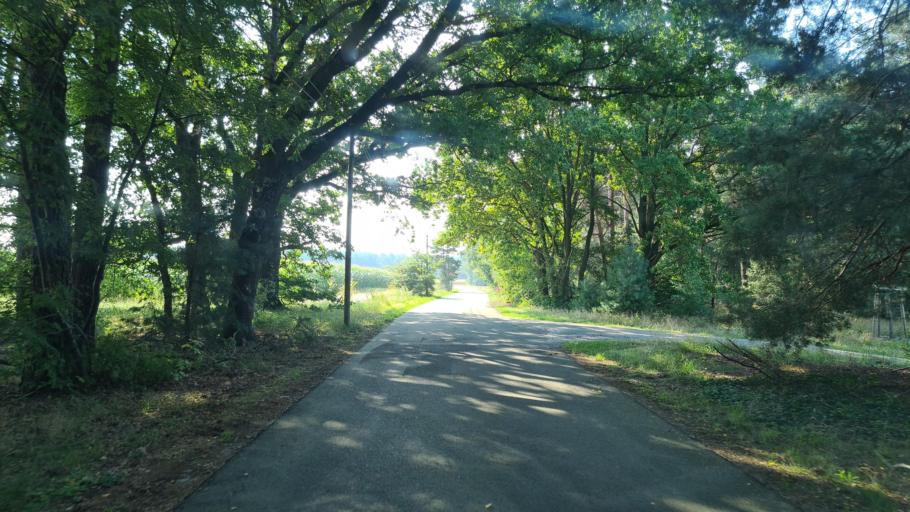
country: DE
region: Brandenburg
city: Luckau
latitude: 51.7777
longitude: 13.6996
